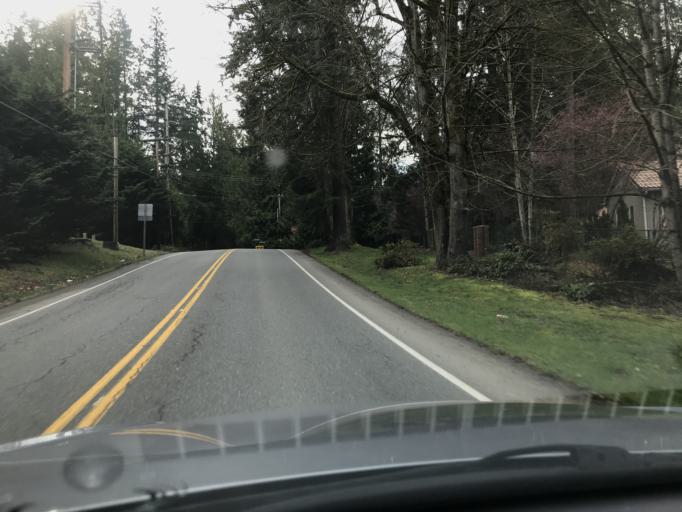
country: US
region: Washington
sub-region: King County
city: Union Hill-Novelty Hill
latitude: 47.6631
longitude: -122.0205
